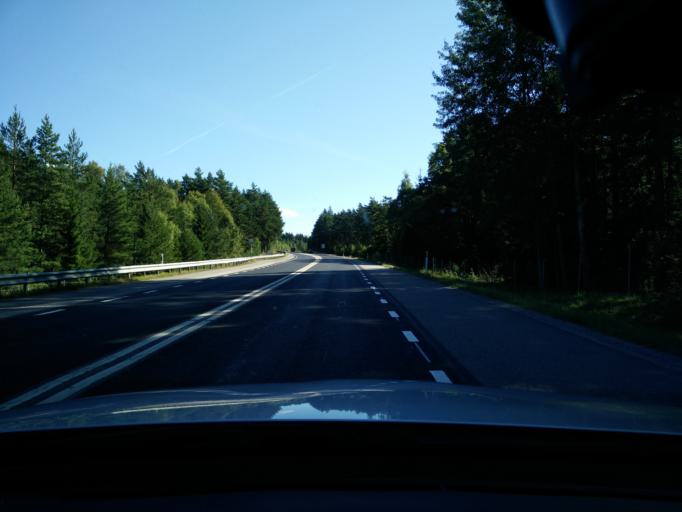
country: SE
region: Stockholm
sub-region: Taby Kommun
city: Taby
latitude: 59.4548
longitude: 18.1528
